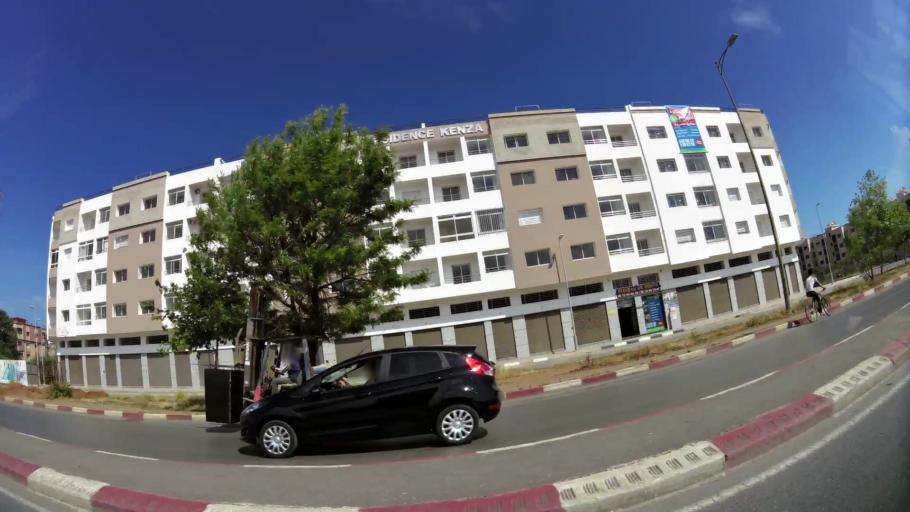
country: MA
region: Rabat-Sale-Zemmour-Zaer
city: Sale
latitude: 34.0616
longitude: -6.8005
